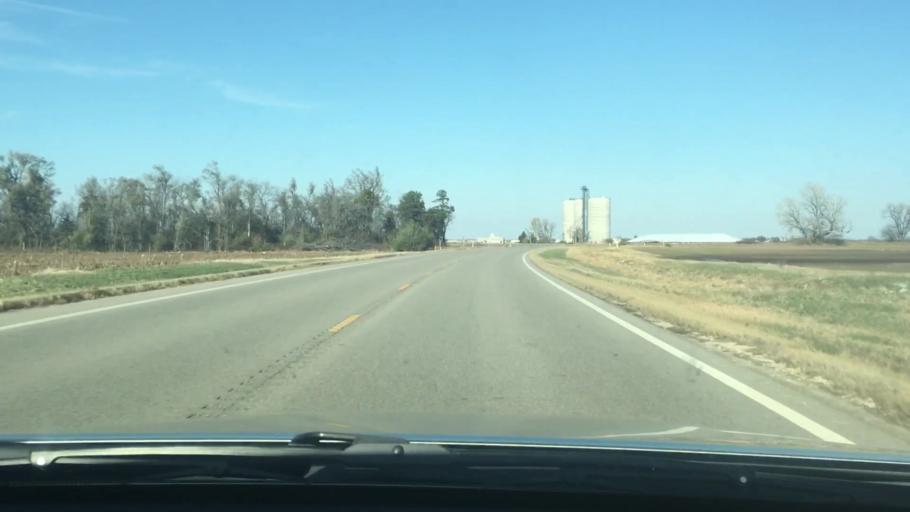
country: US
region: Kansas
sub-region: Rice County
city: Sterling
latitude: 38.2590
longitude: -98.2056
